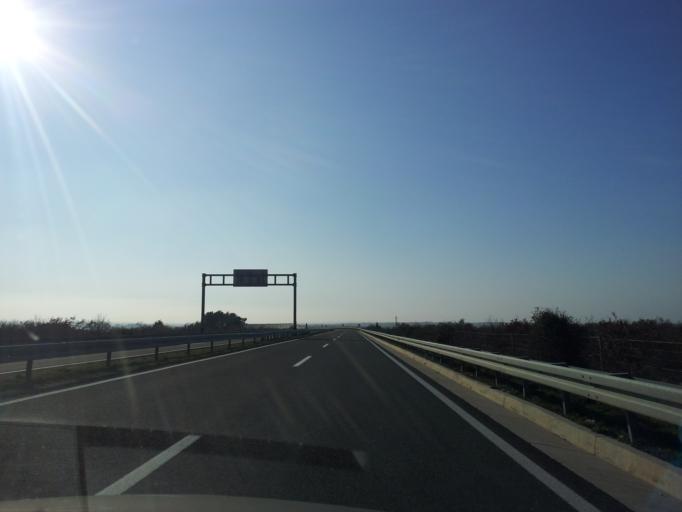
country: HR
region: Zadarska
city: Galovac
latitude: 44.1189
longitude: 15.4252
